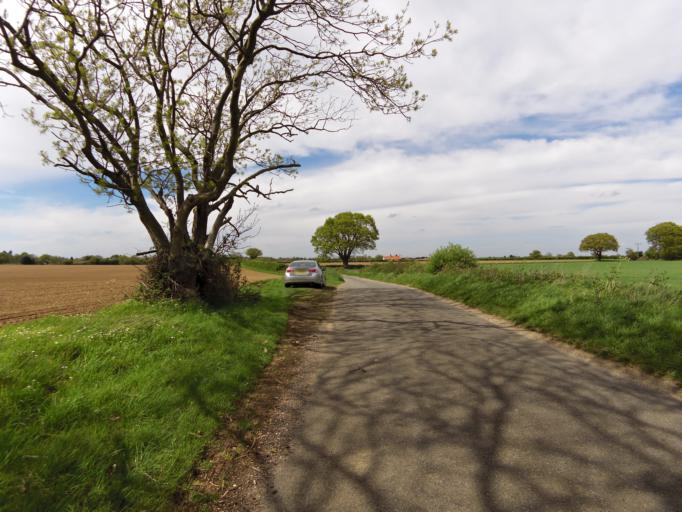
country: GB
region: England
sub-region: Suffolk
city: Ipswich
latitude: 52.0020
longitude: 1.1203
